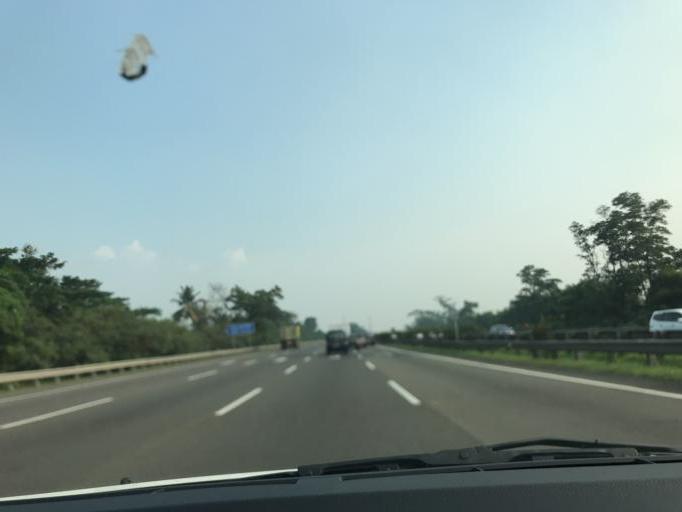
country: ID
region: West Java
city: Citeureup
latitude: -6.4985
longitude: 106.8683
